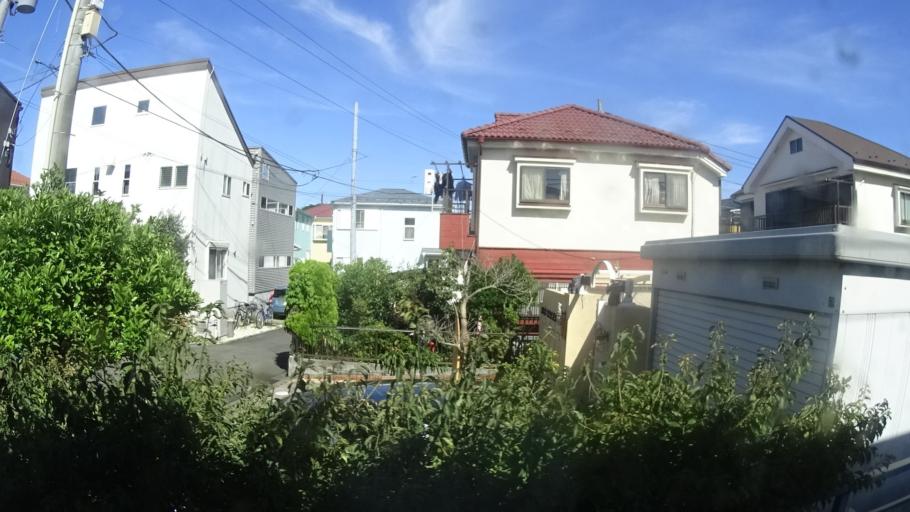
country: JP
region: Kanagawa
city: Fujisawa
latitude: 35.3184
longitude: 139.4825
